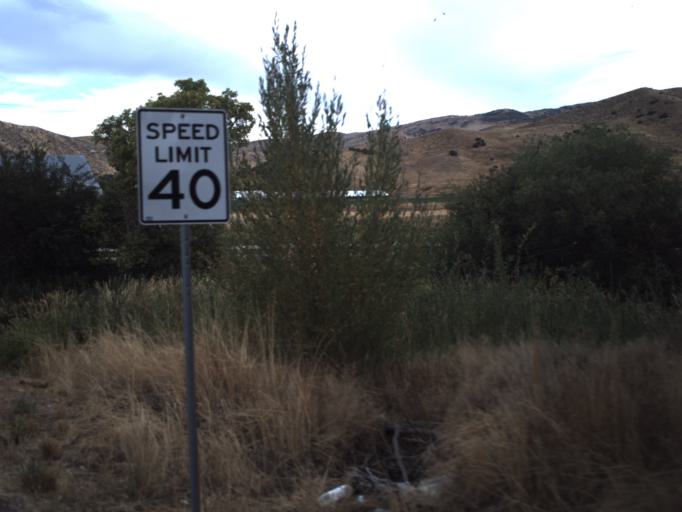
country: US
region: Utah
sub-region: Morgan County
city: Morgan
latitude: 40.9816
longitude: -111.6783
